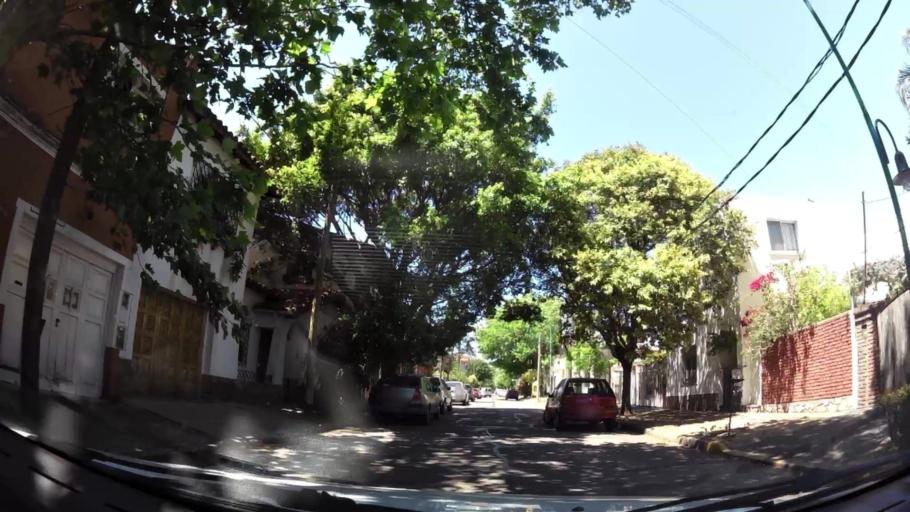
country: AR
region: Buenos Aires
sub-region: Partido de Vicente Lopez
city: Olivos
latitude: -34.5044
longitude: -58.5031
